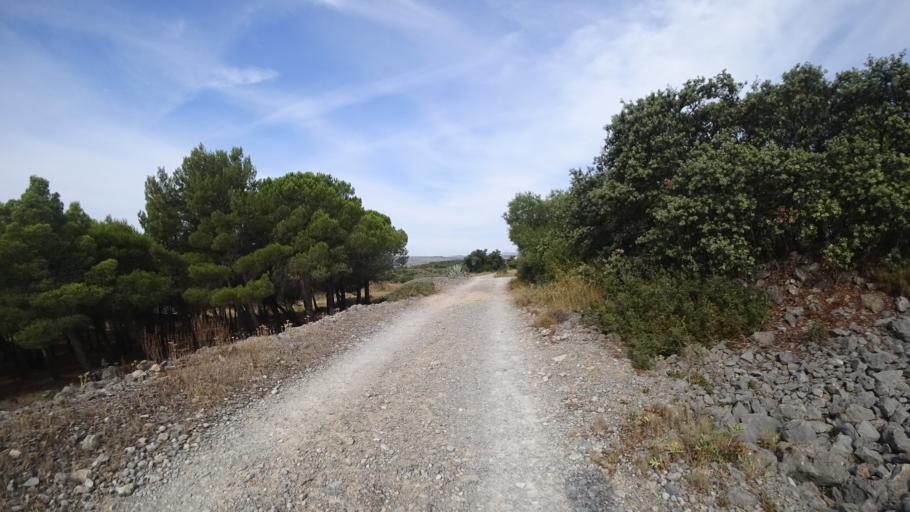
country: FR
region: Languedoc-Roussillon
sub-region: Departement de l'Aude
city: Leucate
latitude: 42.8995
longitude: 3.0343
